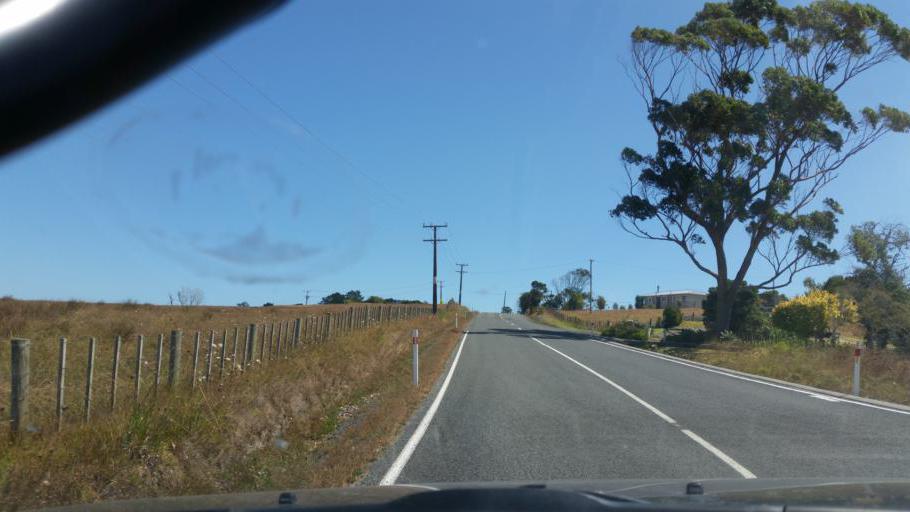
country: NZ
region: Northland
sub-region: Kaipara District
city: Dargaville
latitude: -36.0064
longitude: 173.9478
